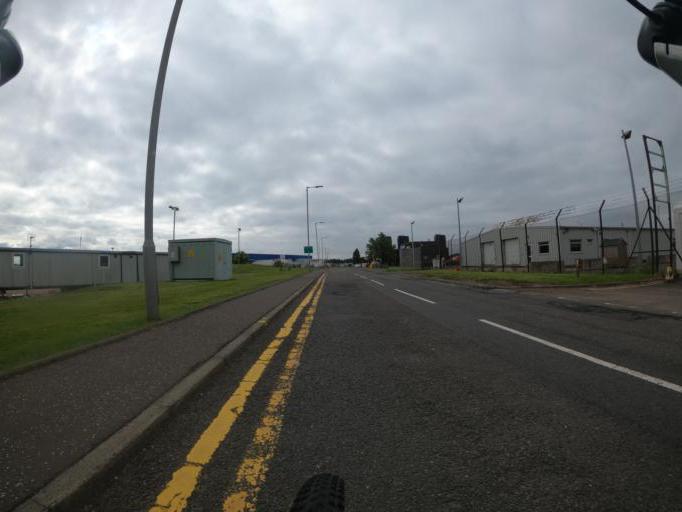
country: GB
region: Scotland
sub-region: Edinburgh
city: Ratho
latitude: 55.9458
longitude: -3.3696
